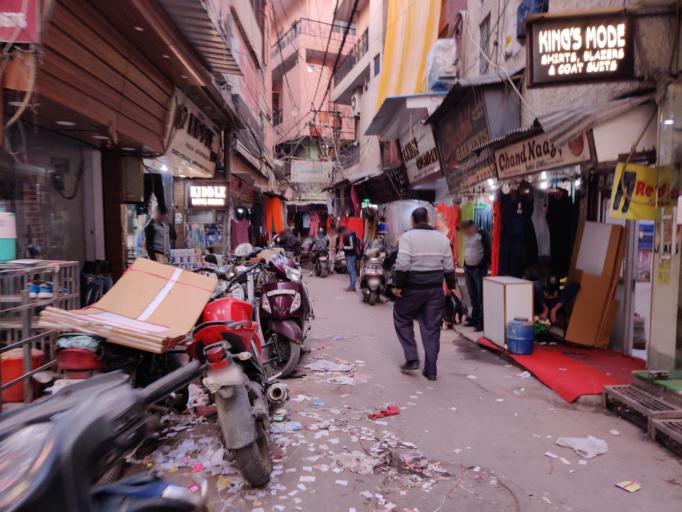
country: IN
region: NCT
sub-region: North Delhi
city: Delhi
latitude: 28.6614
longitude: 77.2655
